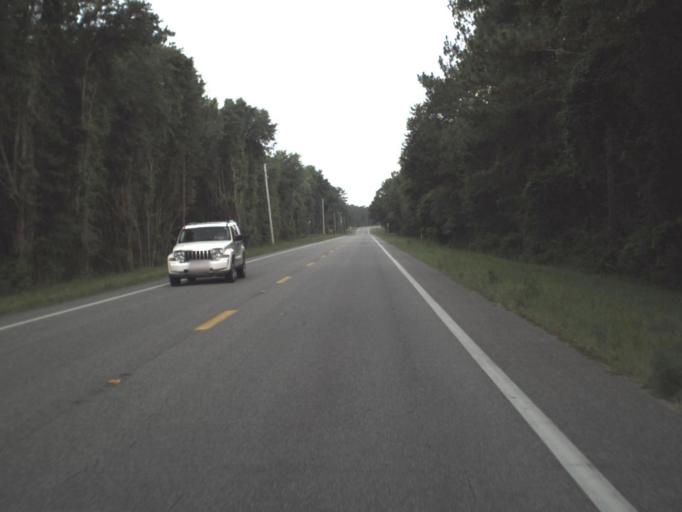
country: US
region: Florida
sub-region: Suwannee County
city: Live Oak
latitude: 30.3918
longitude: -83.1924
